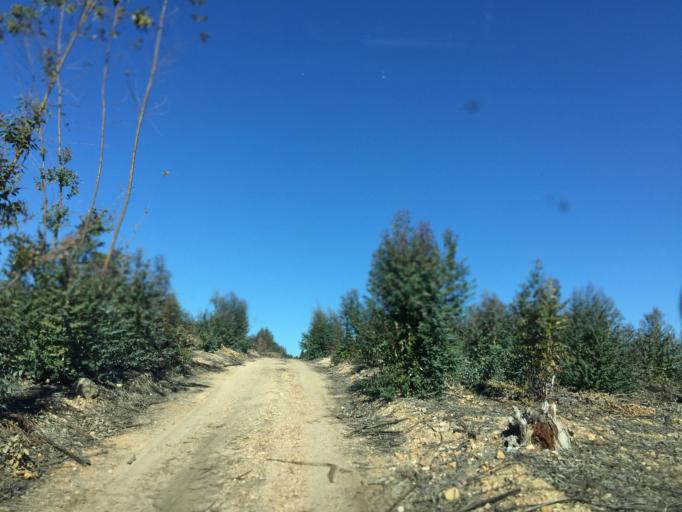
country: PT
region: Portalegre
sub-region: Nisa
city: Nisa
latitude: 39.4920
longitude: -7.7721
